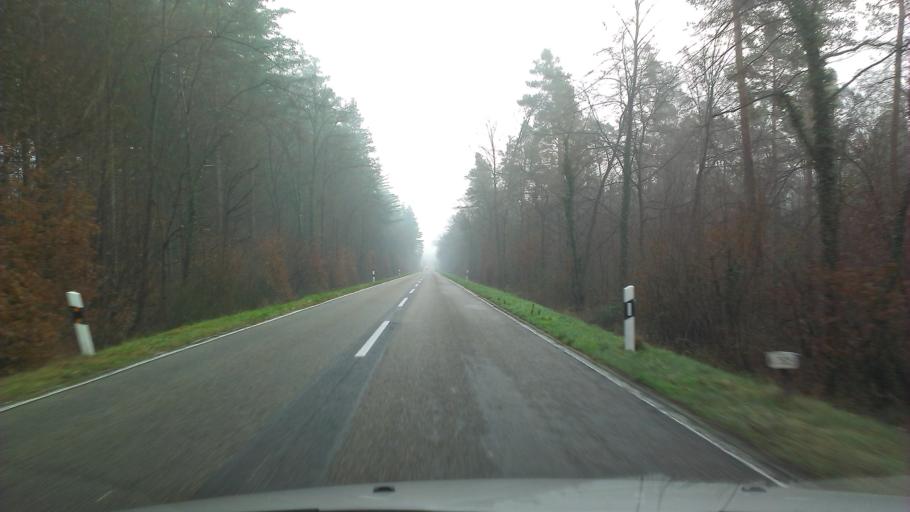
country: DE
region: Baden-Wuerttemberg
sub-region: Karlsruhe Region
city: Graben-Neudorf
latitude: 49.1893
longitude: 8.5111
